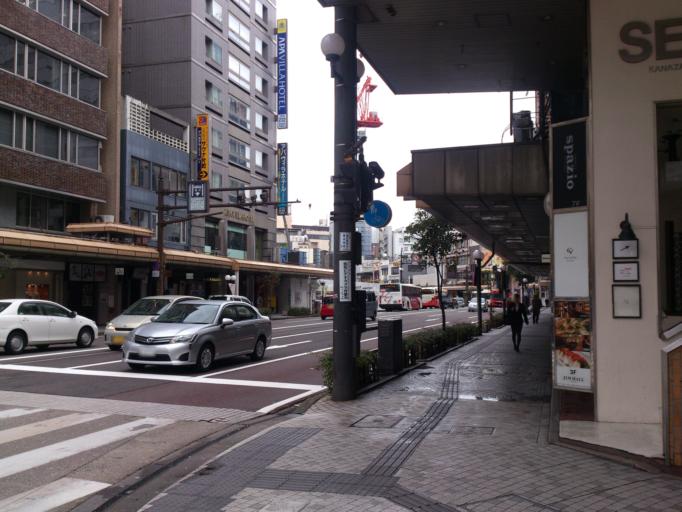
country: JP
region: Ishikawa
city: Kanazawa-shi
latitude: 36.5598
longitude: 136.6521
